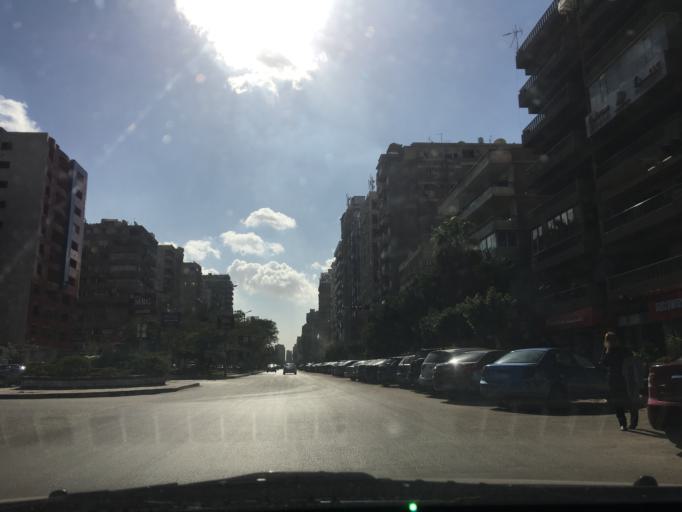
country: EG
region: Muhafazat al Qahirah
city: Cairo
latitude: 30.0606
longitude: 31.3452
